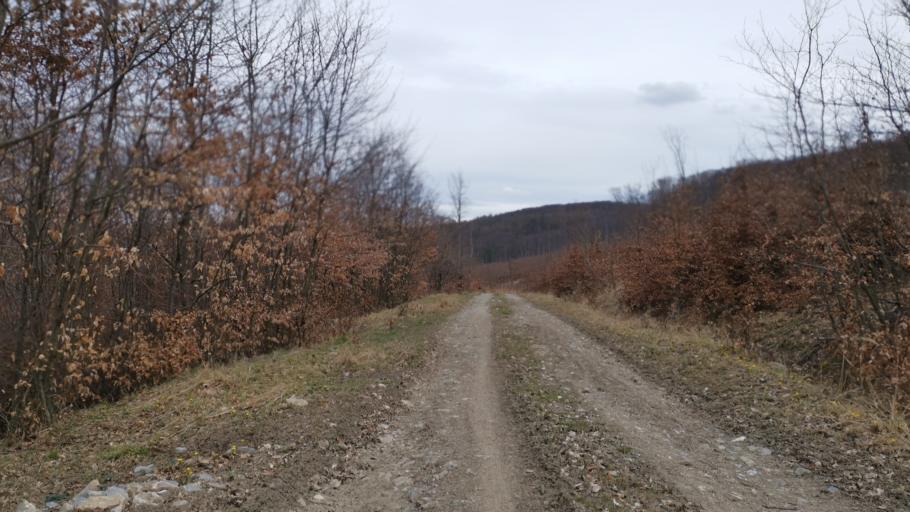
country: CZ
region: South Moravian
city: Knezdub
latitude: 48.8188
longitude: 17.3477
